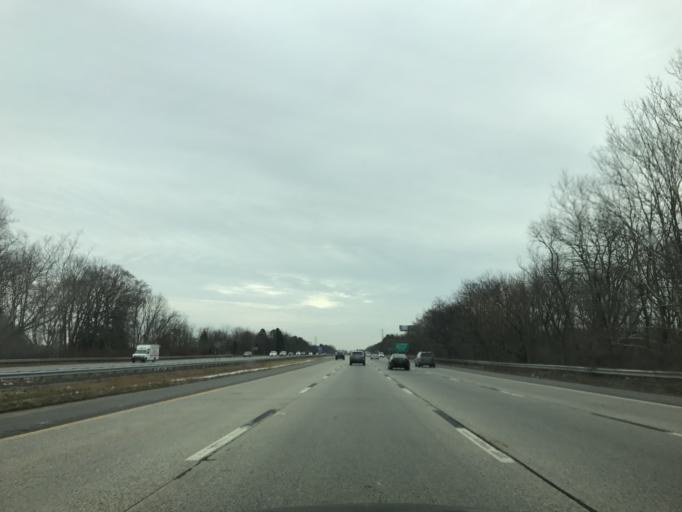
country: US
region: New Jersey
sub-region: Burlington County
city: Willingboro
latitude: 39.9977
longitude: -74.8655
